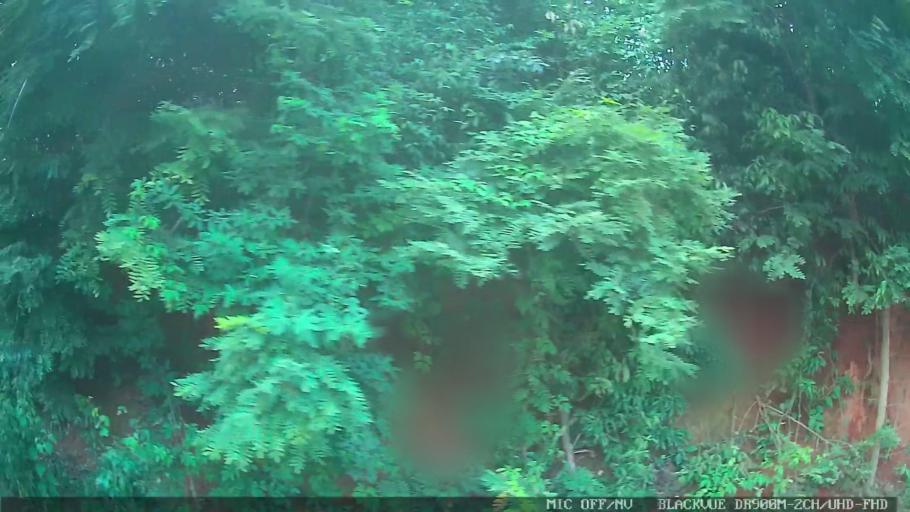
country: BR
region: Minas Gerais
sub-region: Extrema
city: Extrema
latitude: -22.8518
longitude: -46.3038
